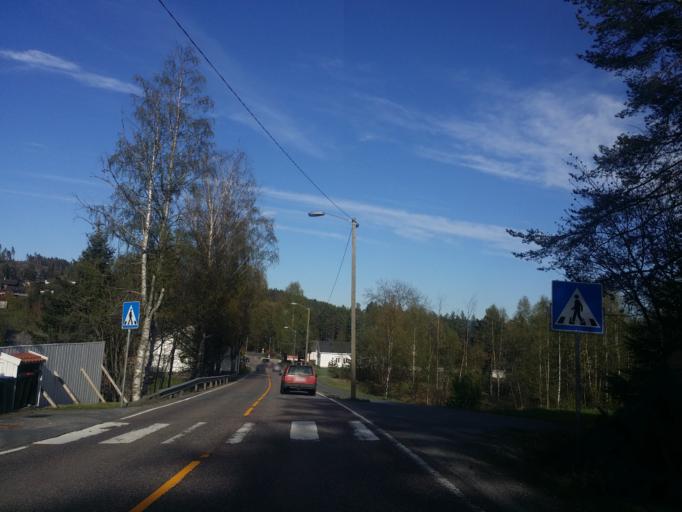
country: NO
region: Buskerud
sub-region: Kongsberg
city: Kongsberg
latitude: 59.6248
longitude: 9.6017
